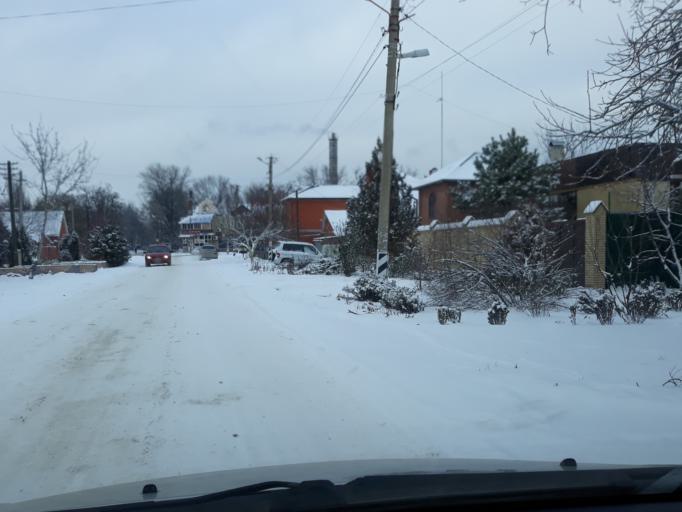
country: RU
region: Rostov
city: Taganrog
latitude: 47.2354
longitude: 38.8832
